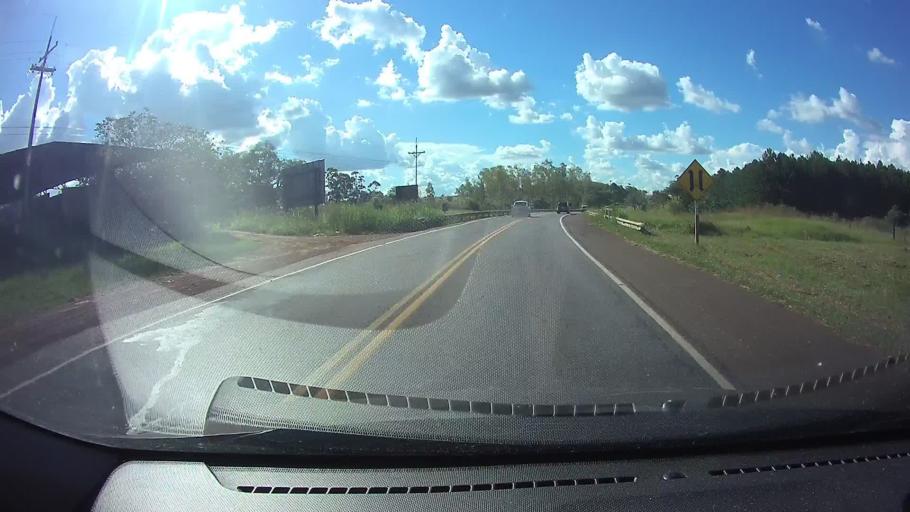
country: PY
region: Cordillera
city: Itacurubi de la Cordillera
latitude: -25.4529
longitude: -56.8990
